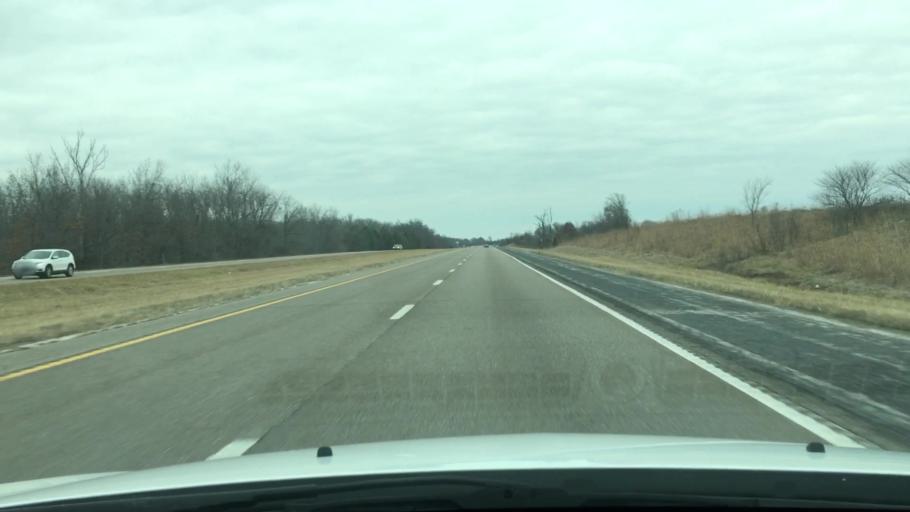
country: US
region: Missouri
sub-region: Callaway County
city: Fulton
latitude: 38.9899
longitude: -91.8937
